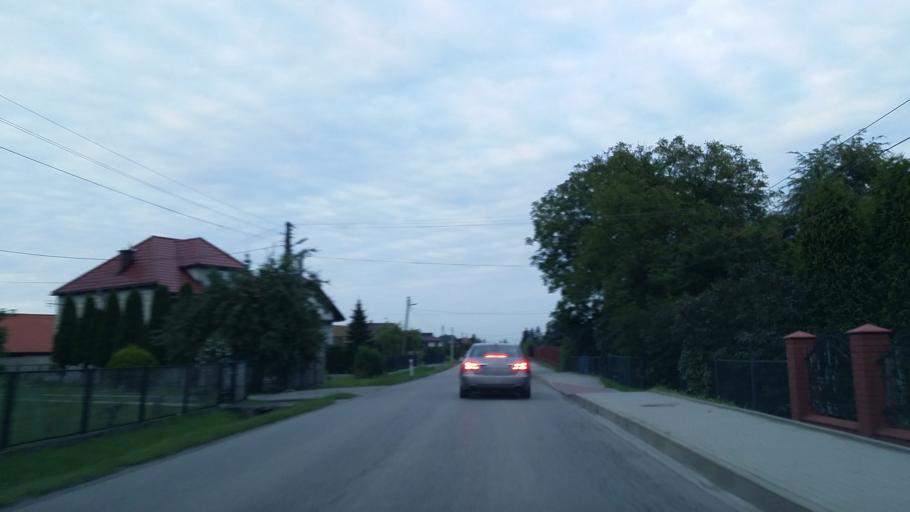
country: PL
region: Lesser Poland Voivodeship
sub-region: Powiat krakowski
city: Kaszow
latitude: 50.0171
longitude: 19.7207
